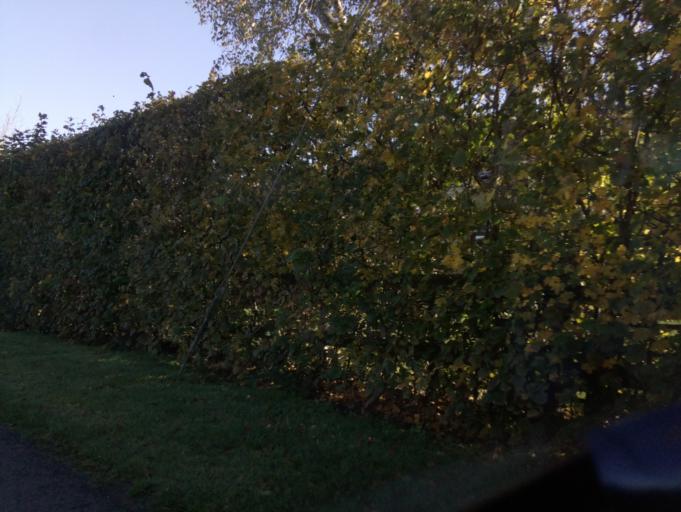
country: GB
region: England
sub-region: Somerset
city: Martock
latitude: 50.9883
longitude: -2.7652
